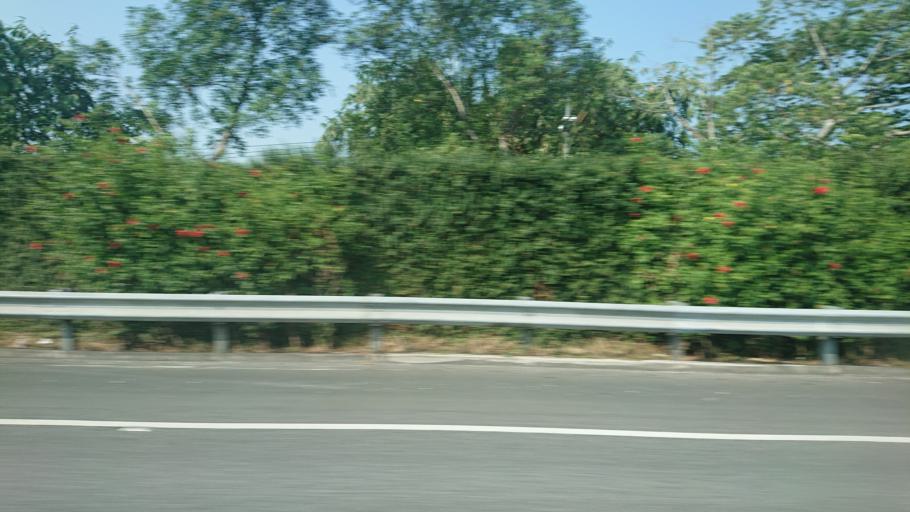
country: TW
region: Taiwan
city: Lugu
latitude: 23.7859
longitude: 120.7044
